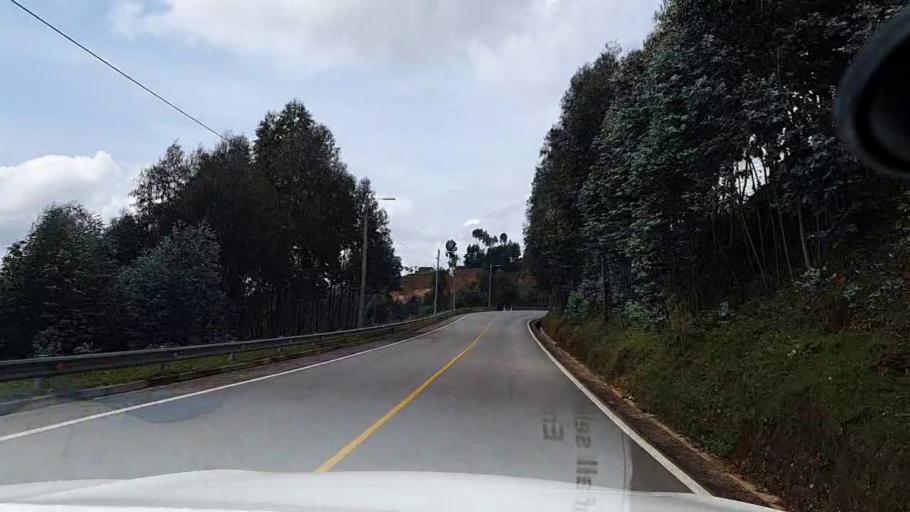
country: RW
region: Southern Province
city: Nzega
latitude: -2.5171
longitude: 29.4605
